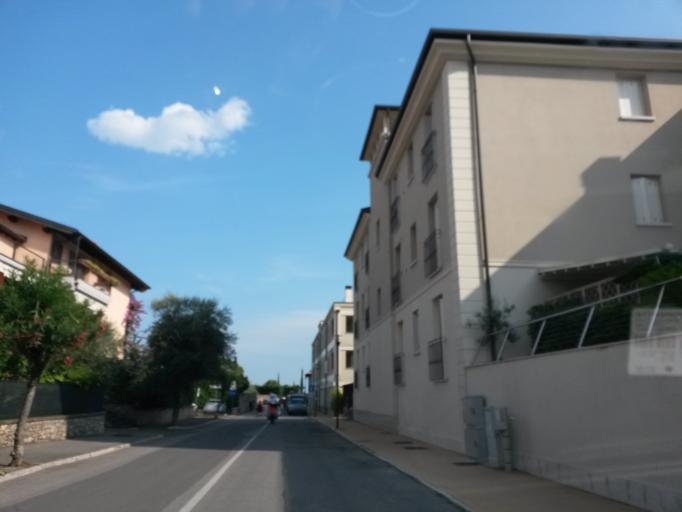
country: IT
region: Lombardy
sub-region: Provincia di Brescia
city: Toscolano Maderno
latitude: 45.6325
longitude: 10.6115
